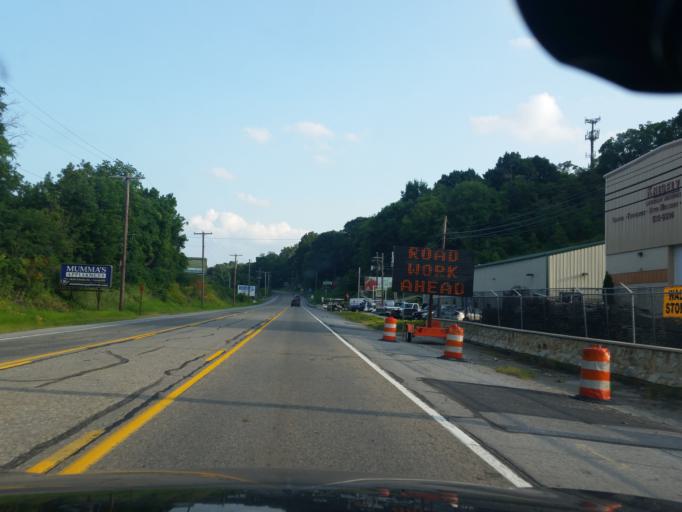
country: US
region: Pennsylvania
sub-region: Cumberland County
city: Enola
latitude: 40.2891
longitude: -76.9298
